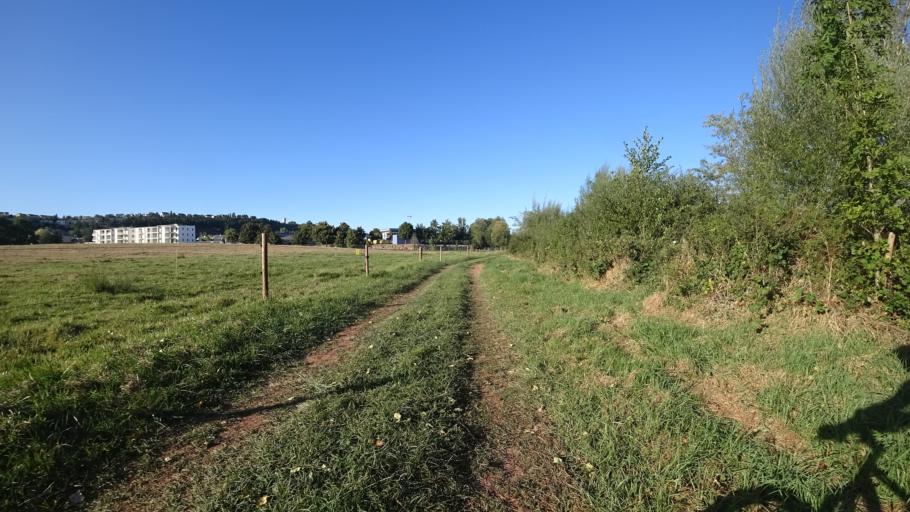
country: FR
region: Midi-Pyrenees
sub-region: Departement de l'Aveyron
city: Rodez
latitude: 44.3703
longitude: 2.5807
